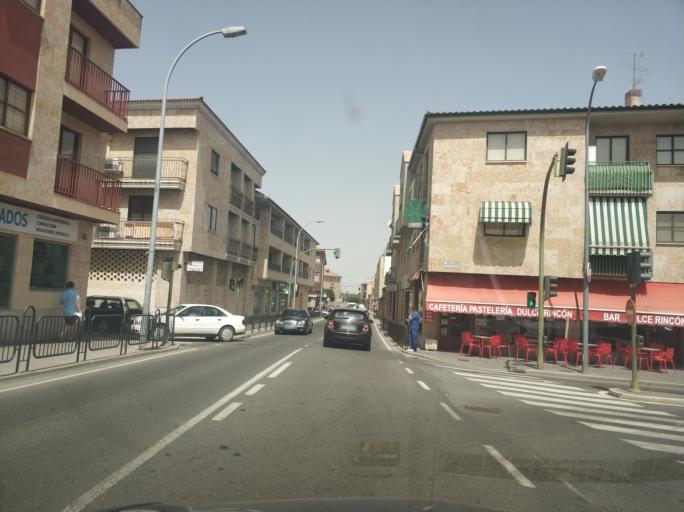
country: ES
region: Castille and Leon
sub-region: Provincia de Salamanca
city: Villamayor
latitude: 40.9986
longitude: -5.6956
